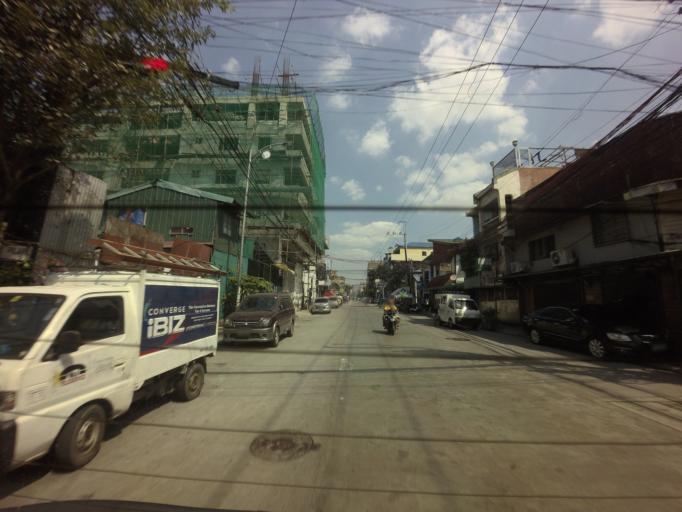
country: PH
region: Metro Manila
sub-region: City of Manila
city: Manila
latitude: 14.6122
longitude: 120.9687
